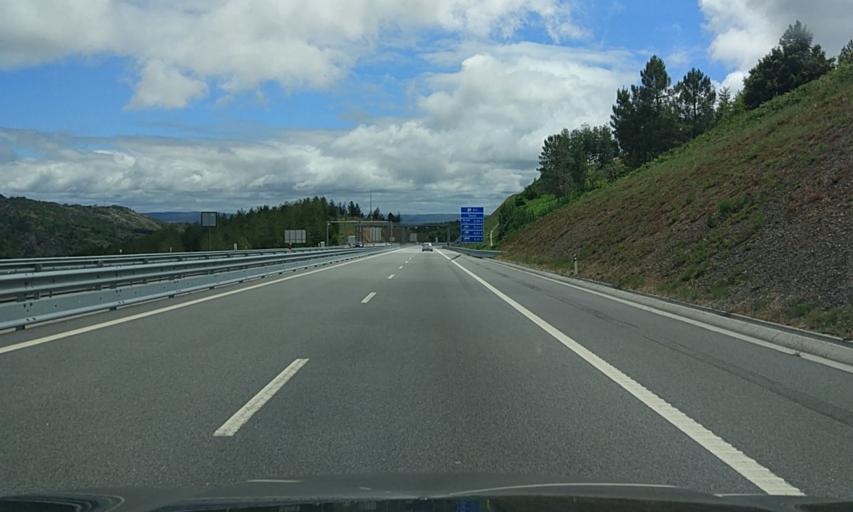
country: PT
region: Vila Real
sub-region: Santa Marta de Penaguiao
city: Santa Marta de Penaguiao
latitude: 41.2781
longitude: -7.8444
